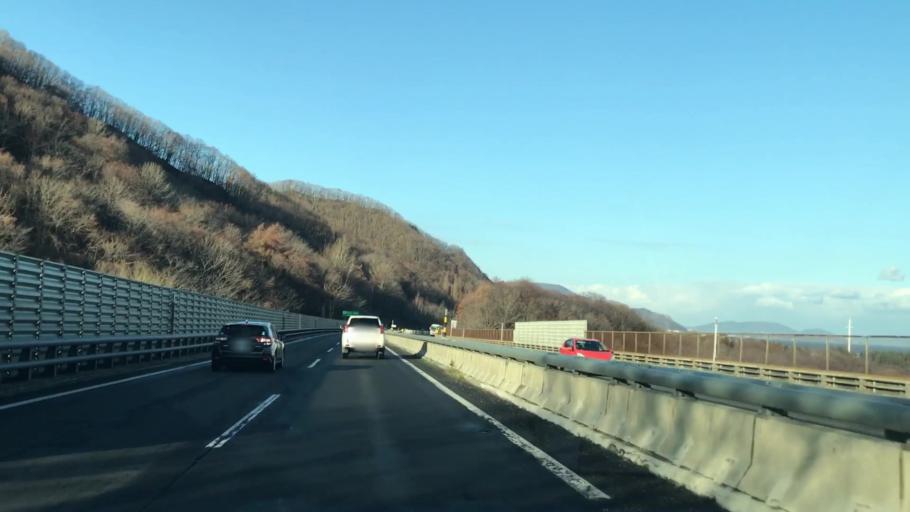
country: JP
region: Hokkaido
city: Sapporo
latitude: 43.1259
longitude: 141.2007
